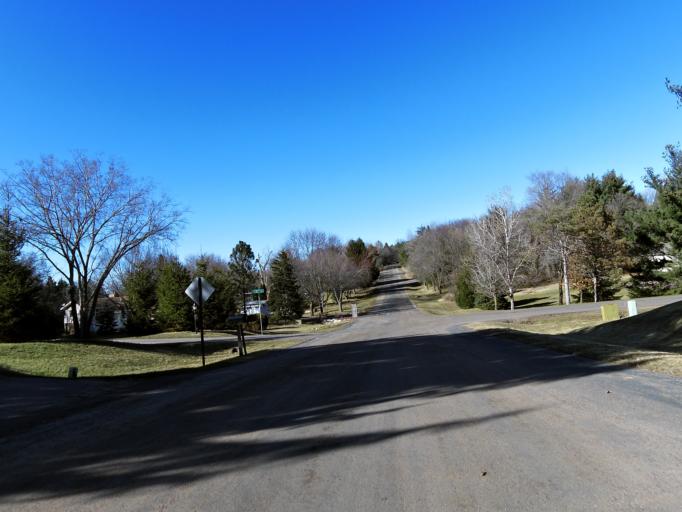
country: US
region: Minnesota
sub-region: Washington County
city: Lake Elmo
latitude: 44.9793
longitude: -92.8263
